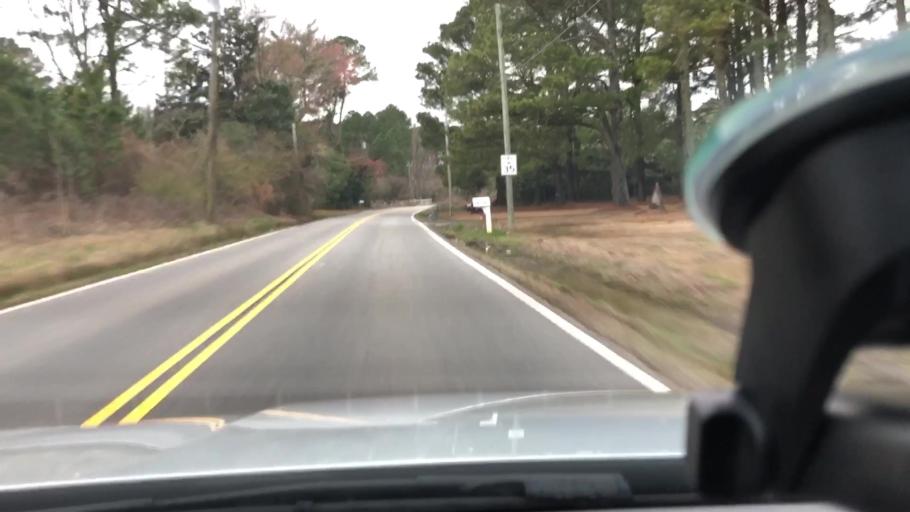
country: US
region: Virginia
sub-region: City of Virginia Beach
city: Virginia Beach
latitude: 36.7306
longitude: -75.9799
